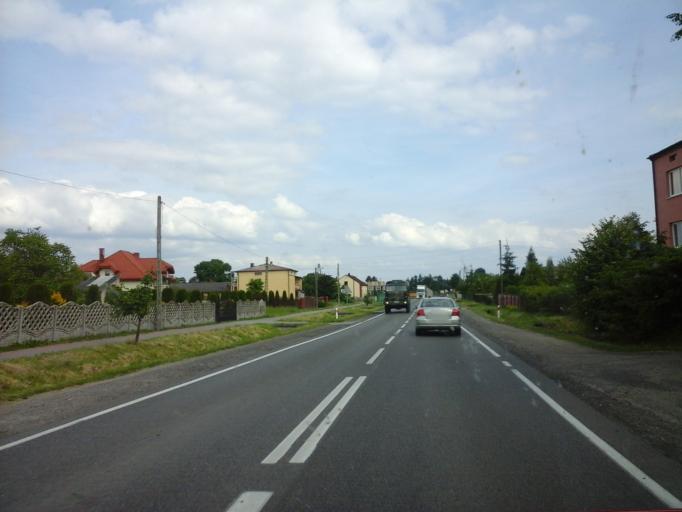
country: PL
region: Lodz Voivodeship
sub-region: Powiat opoczynski
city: Mniszkow
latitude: 51.3300
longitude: 20.0334
